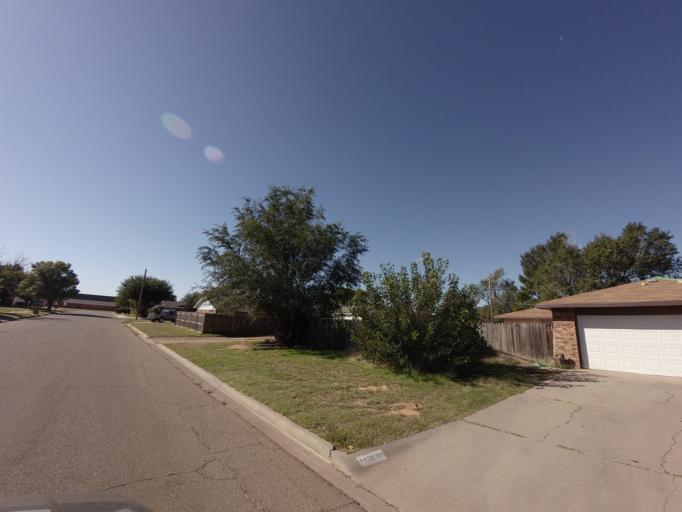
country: US
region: New Mexico
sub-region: Curry County
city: Clovis
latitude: 34.4304
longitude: -103.2234
